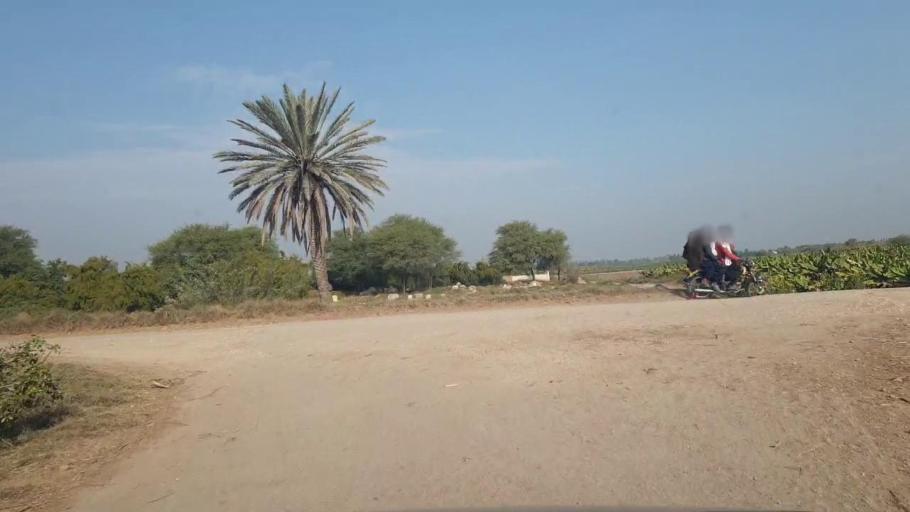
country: PK
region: Sindh
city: Tando Adam
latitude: 25.7531
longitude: 68.6068
